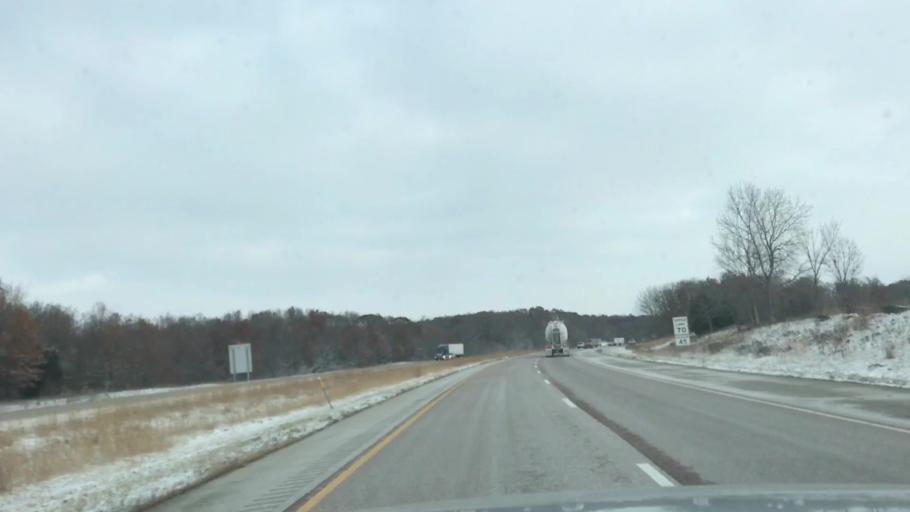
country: US
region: Illinois
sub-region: Macoupin County
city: Mount Olive
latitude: 39.0809
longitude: -89.7549
